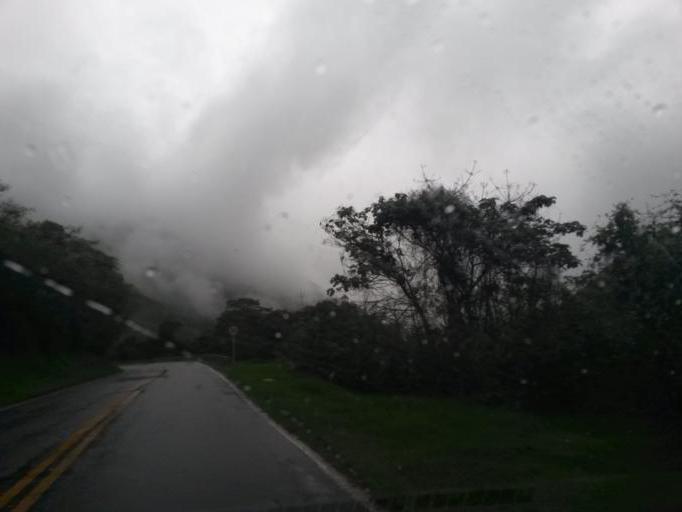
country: CO
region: Cauca
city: Popayan
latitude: 2.3771
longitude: -76.4937
